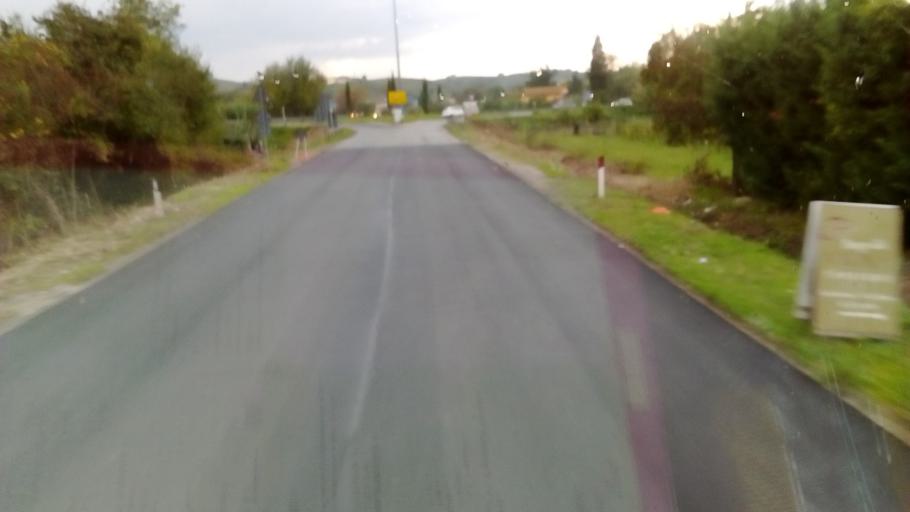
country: IT
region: Tuscany
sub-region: Province of Florence
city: Castelfiorentino
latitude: 43.5926
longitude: 10.9740
